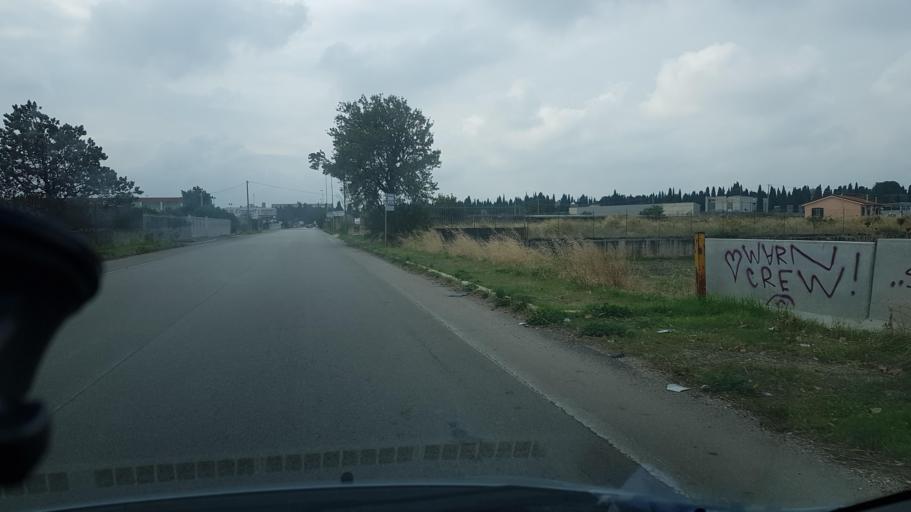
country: IT
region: Apulia
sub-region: Provincia di Foggia
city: Foggia
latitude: 41.4778
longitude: 15.5533
